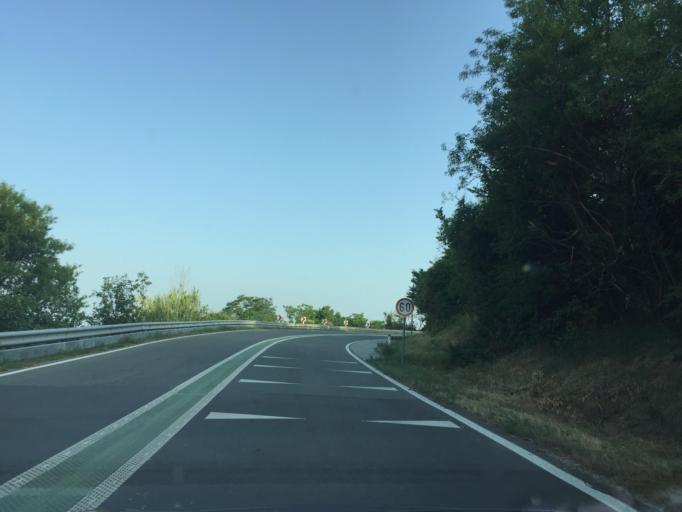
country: SI
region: Koper-Capodistria
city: Sv. Anton
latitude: 45.5493
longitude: 13.8781
